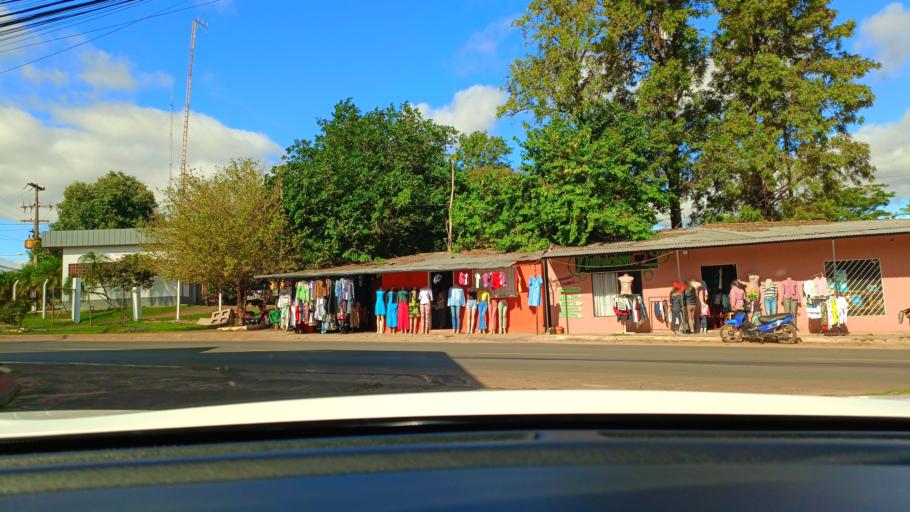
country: PY
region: San Pedro
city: Guayaybi
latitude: -24.6743
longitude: -56.4438
